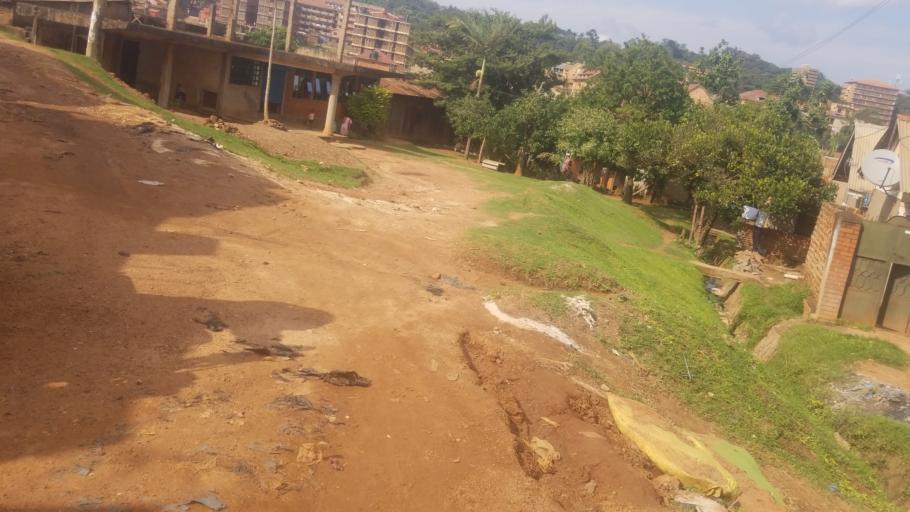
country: UG
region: Central Region
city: Kampala Central Division
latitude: 0.3309
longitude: 32.5597
